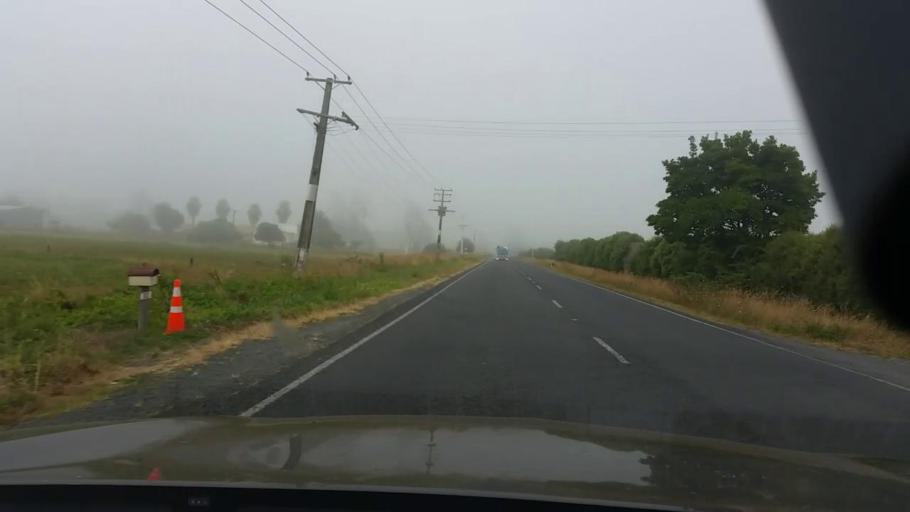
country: NZ
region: Waikato
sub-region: Hamilton City
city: Hamilton
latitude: -37.6344
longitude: 175.3044
